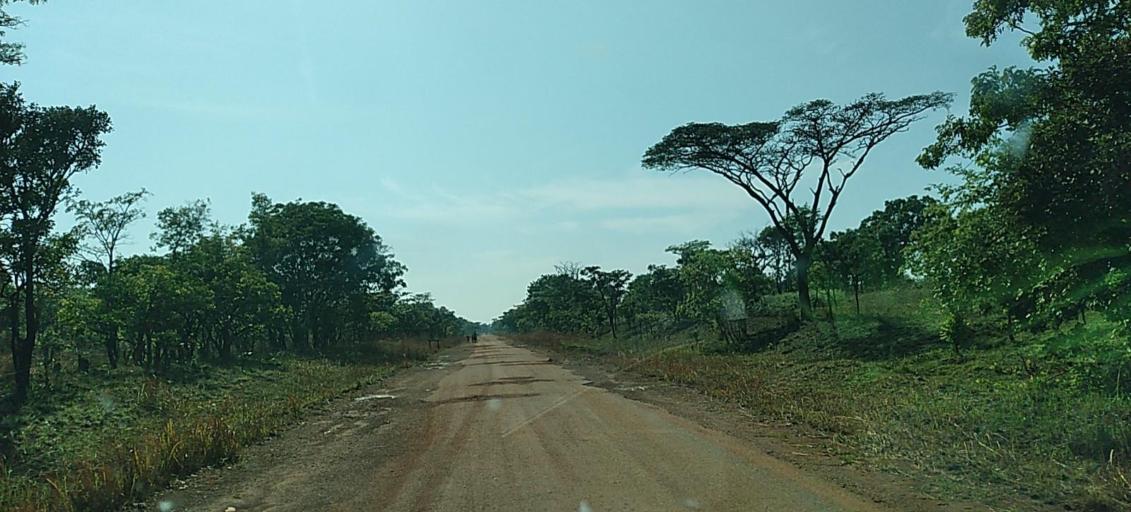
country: ZM
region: North-Western
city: Mwinilunga
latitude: -11.7896
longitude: 25.0604
